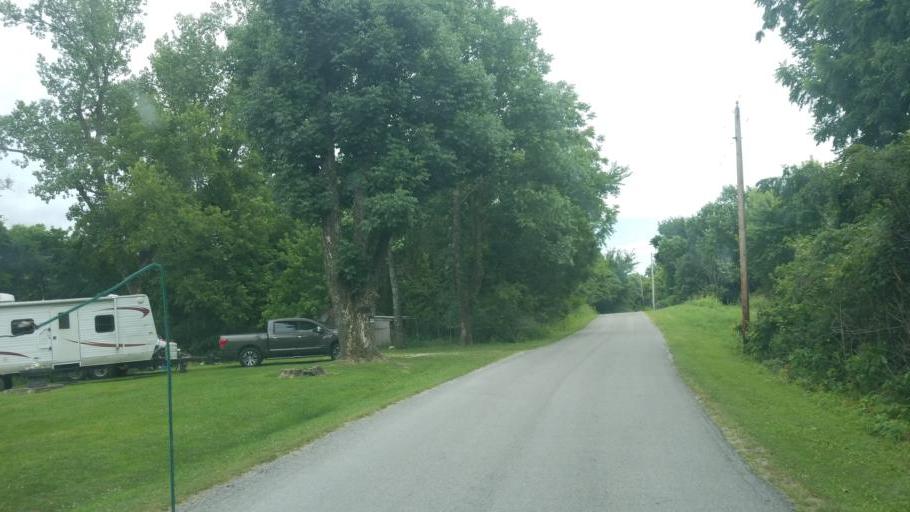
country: US
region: Illinois
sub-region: Jackson County
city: Murphysboro
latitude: 37.6753
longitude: -89.3912
